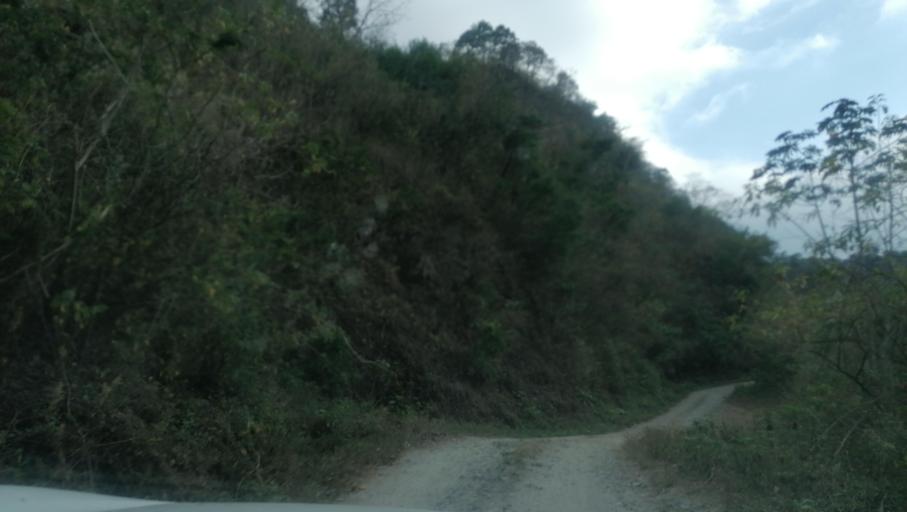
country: MX
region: Chiapas
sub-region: Cacahoatan
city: Benito Juarez
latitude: 15.1615
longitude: -92.1772
